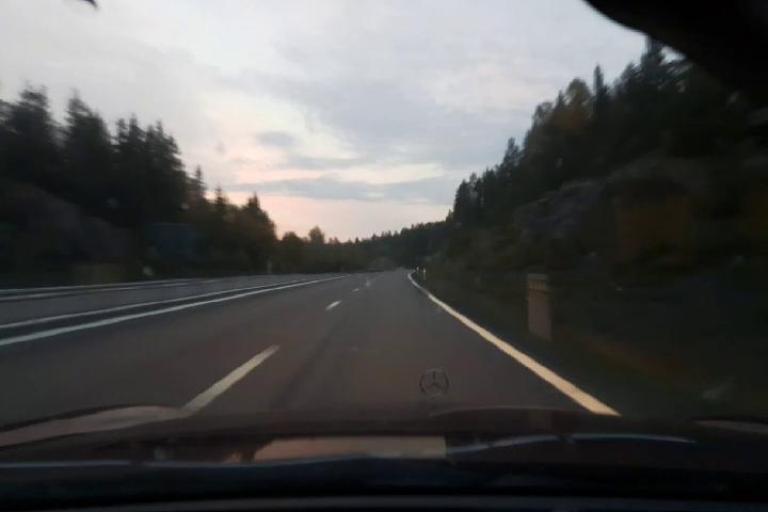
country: SE
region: Vaesternorrland
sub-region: Kramfors Kommun
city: Nordingra
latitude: 62.9429
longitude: 18.0941
